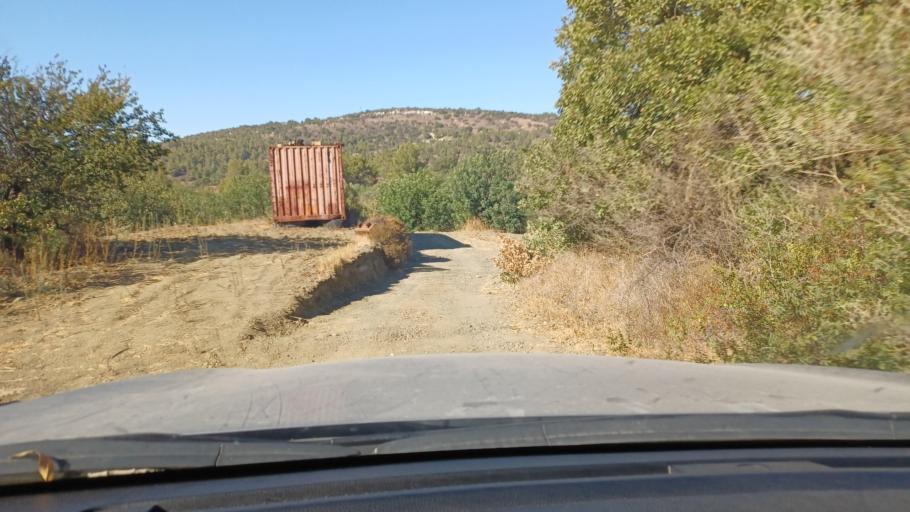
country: CY
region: Pafos
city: Polis
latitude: 35.0111
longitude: 32.5026
